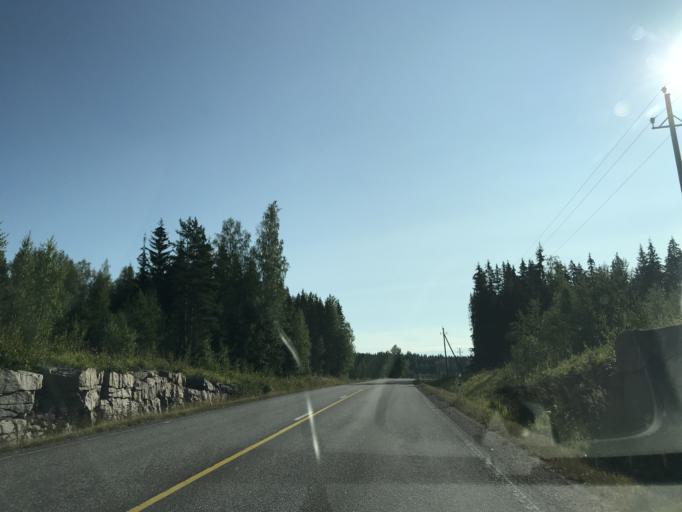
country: FI
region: Paijanne Tavastia
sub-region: Lahti
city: Orimattila
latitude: 60.7892
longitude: 25.6372
